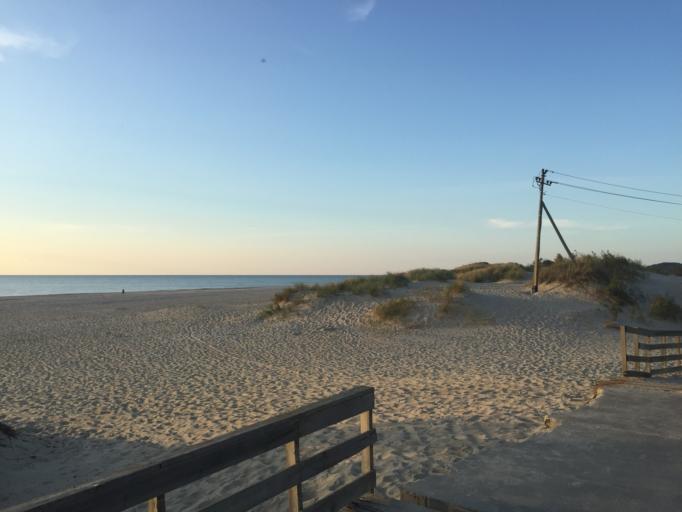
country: RU
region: Kaliningrad
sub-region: Gorod Kaliningrad
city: Yantarnyy
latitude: 54.8753
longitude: 19.9328
